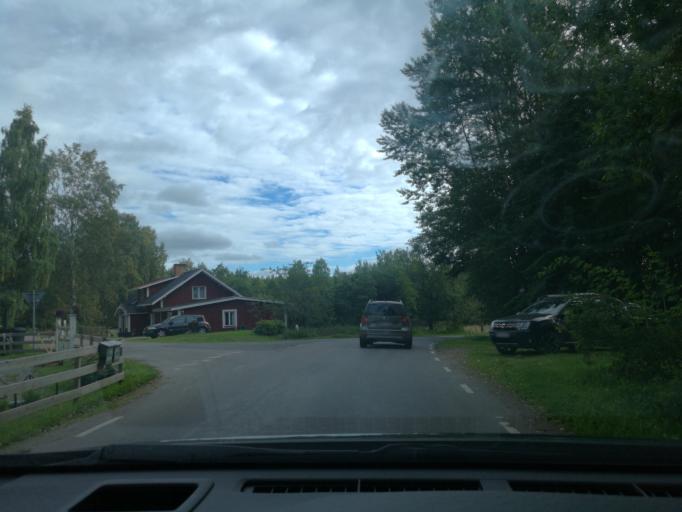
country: SE
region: OEstergoetland
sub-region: Soderkopings Kommun
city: Soederkoeping
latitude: 58.5087
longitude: 16.4328
